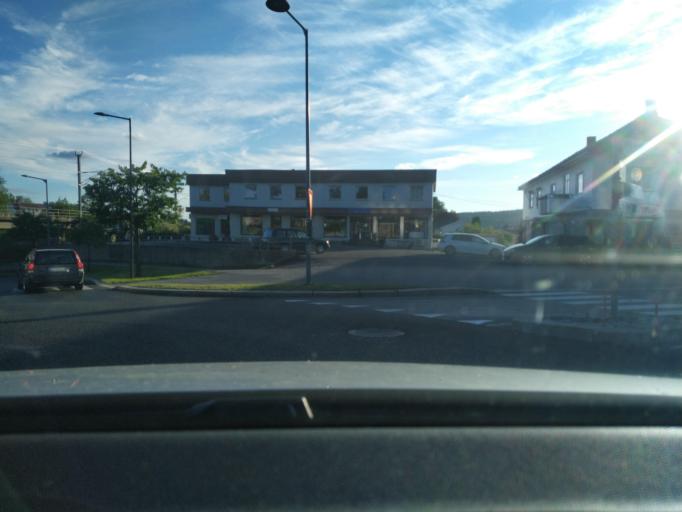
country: NO
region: Akershus
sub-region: Sorum
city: Sorumsand
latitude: 59.9858
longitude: 11.2379
